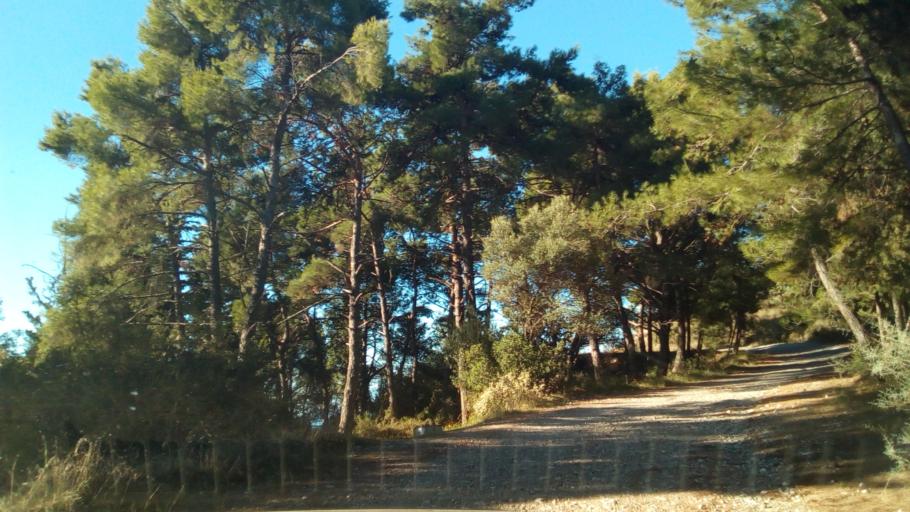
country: GR
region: West Greece
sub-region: Nomos Aitolias kai Akarnanias
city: Nafpaktos
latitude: 38.3977
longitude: 21.8236
